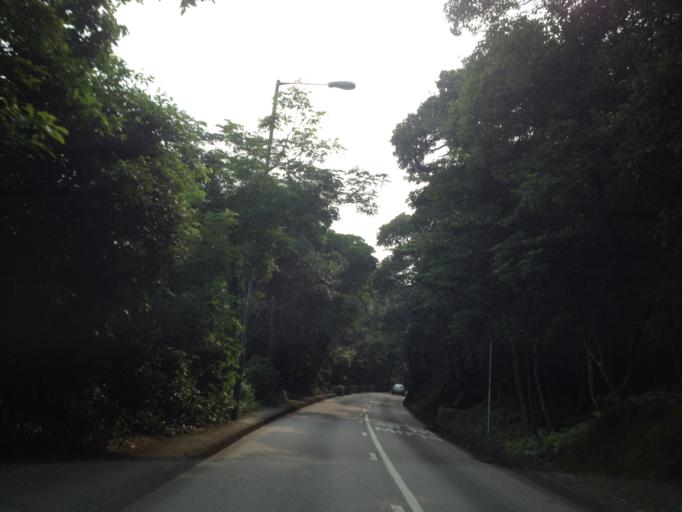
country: HK
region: Wanchai
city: Wan Chai
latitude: 22.2579
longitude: 114.2262
